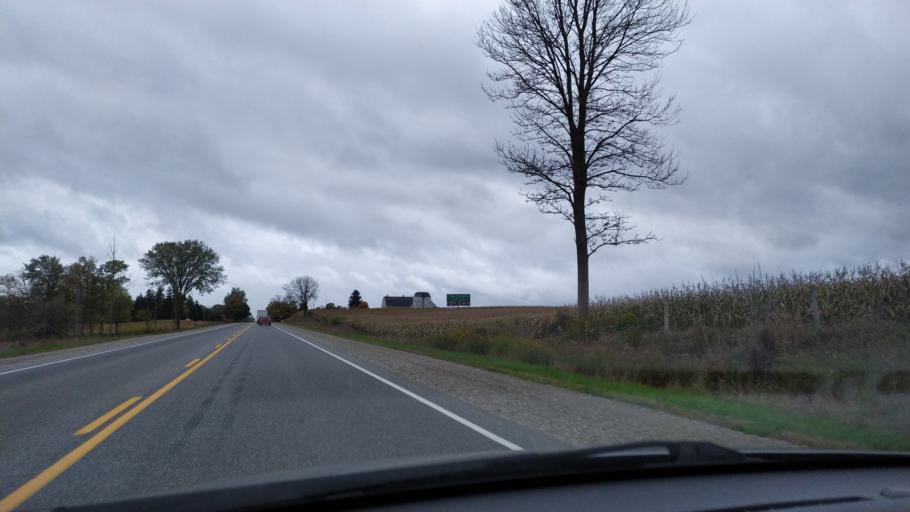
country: CA
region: Ontario
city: Stratford
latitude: 43.3692
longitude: -80.7948
